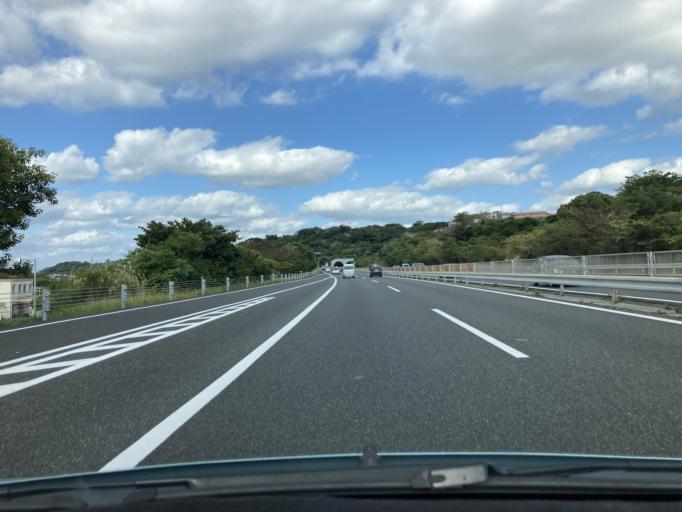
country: JP
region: Okinawa
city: Chatan
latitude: 26.3024
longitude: 127.7917
